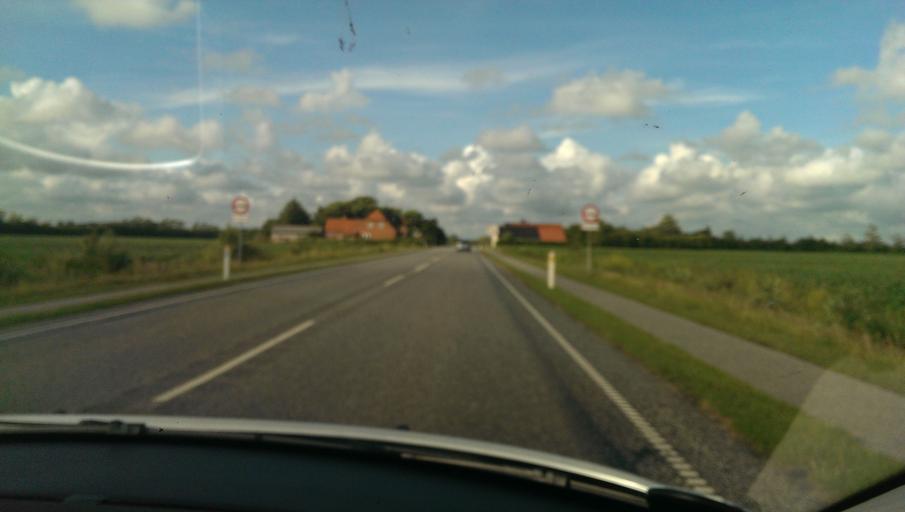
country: DK
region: Central Jutland
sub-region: Ringkobing-Skjern Kommune
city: Ringkobing
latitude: 56.1209
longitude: 8.2752
